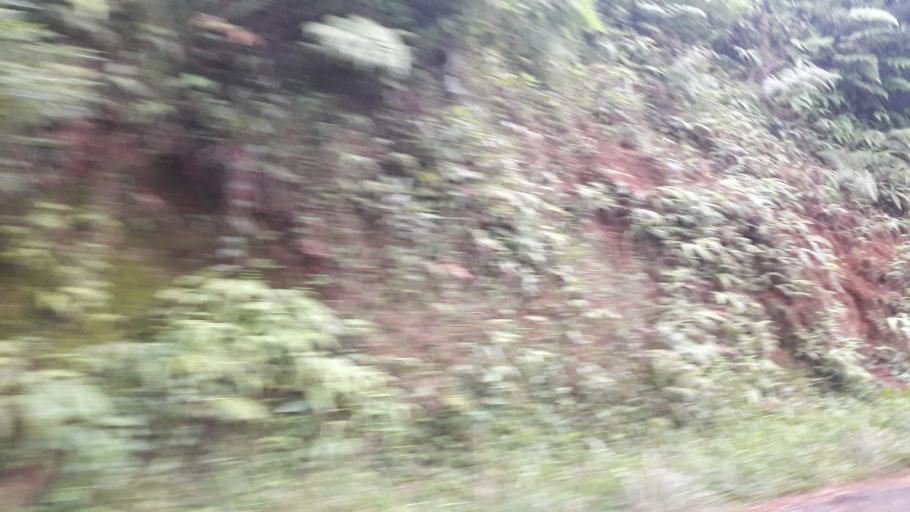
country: ID
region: West Java
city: Cipeundeuy
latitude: -6.6792
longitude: 106.5201
